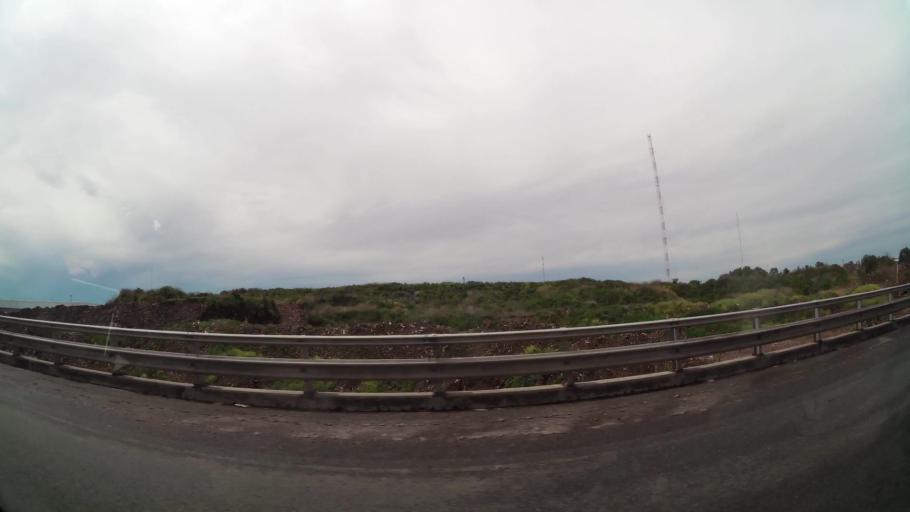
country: AR
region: Buenos Aires F.D.
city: Villa Lugano
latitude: -34.6727
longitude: -58.4375
